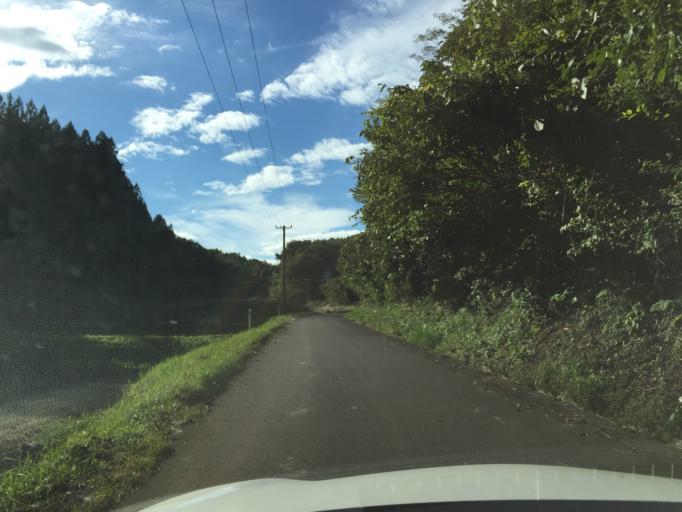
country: JP
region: Fukushima
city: Ishikawa
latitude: 37.1696
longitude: 140.4931
